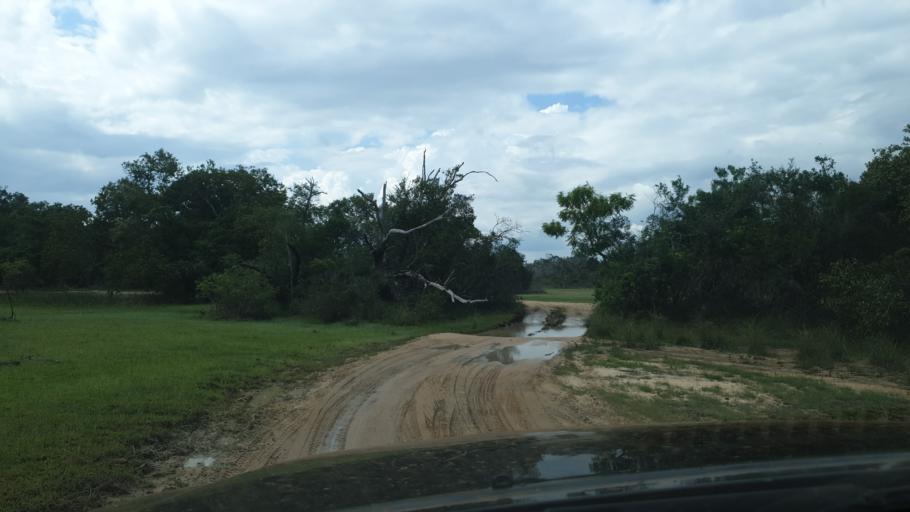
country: LK
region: North Western
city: Puttalam
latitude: 8.4151
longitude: 79.9972
